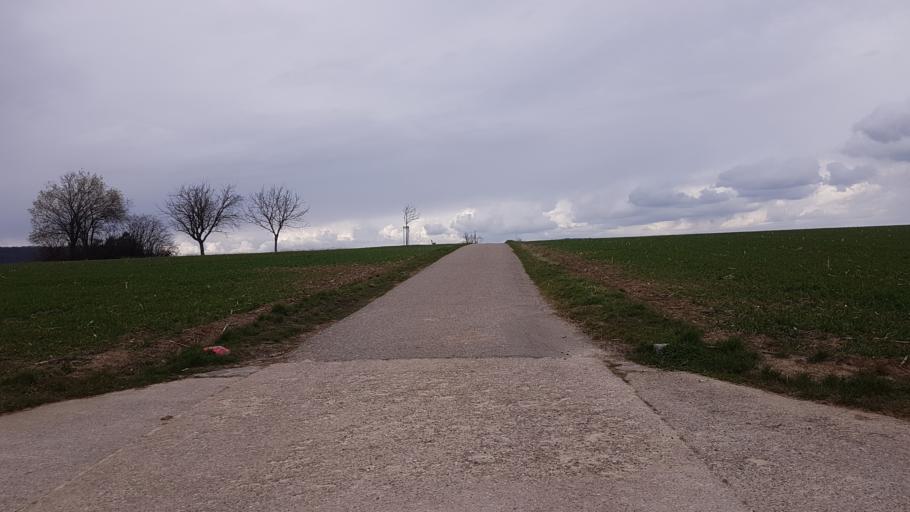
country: DE
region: Baden-Wuerttemberg
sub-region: Regierungsbezirk Stuttgart
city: Brackenheim
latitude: 49.0895
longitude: 9.0952
